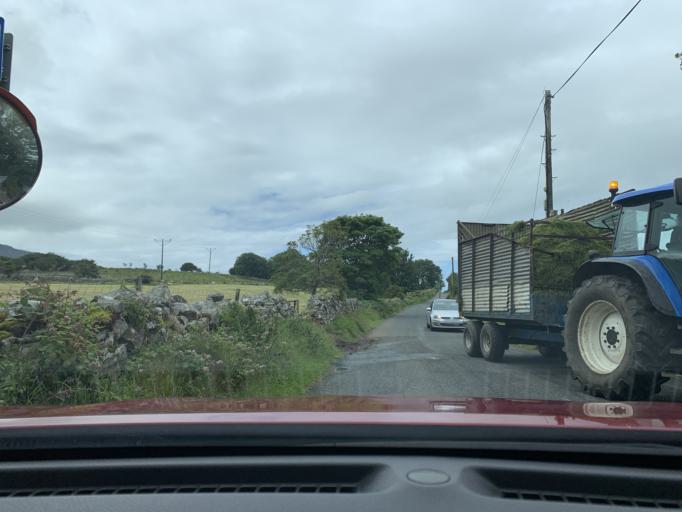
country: IE
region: Connaught
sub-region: Sligo
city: Sligo
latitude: 54.3962
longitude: -8.4414
